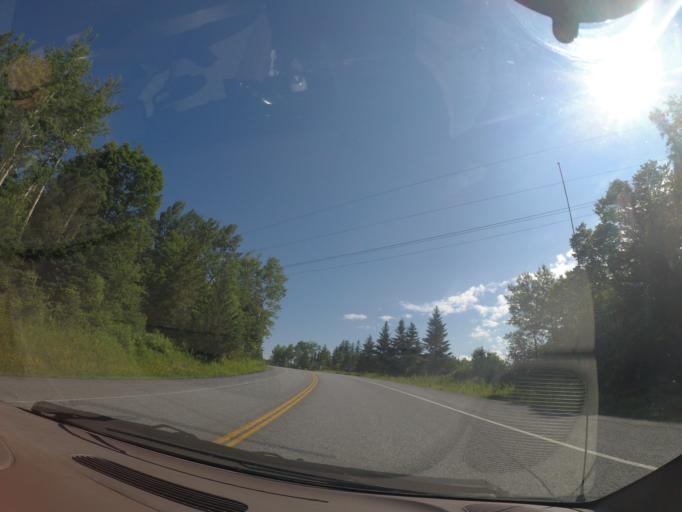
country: US
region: Vermont
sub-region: Bennington County
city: Bennington
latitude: 42.8747
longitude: -73.0821
